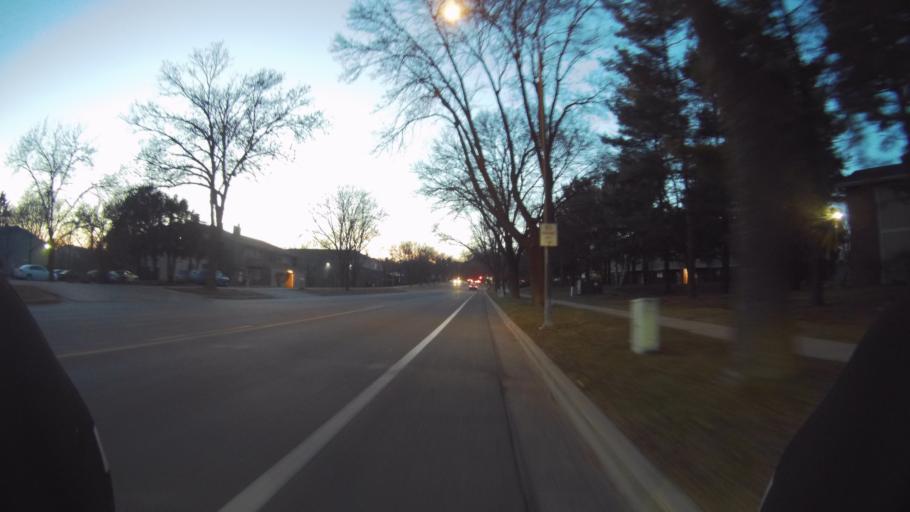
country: US
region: Wisconsin
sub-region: Dane County
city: Middleton
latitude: 43.0463
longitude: -89.5001
